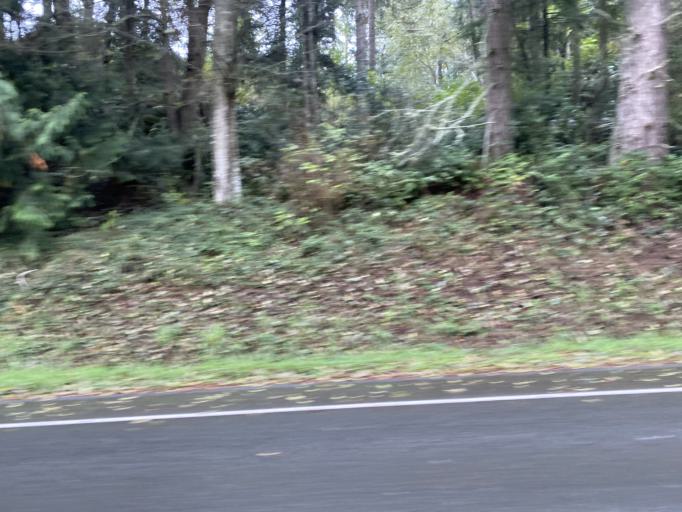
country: US
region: Washington
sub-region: Island County
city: Langley
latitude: 48.0528
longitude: -122.4517
